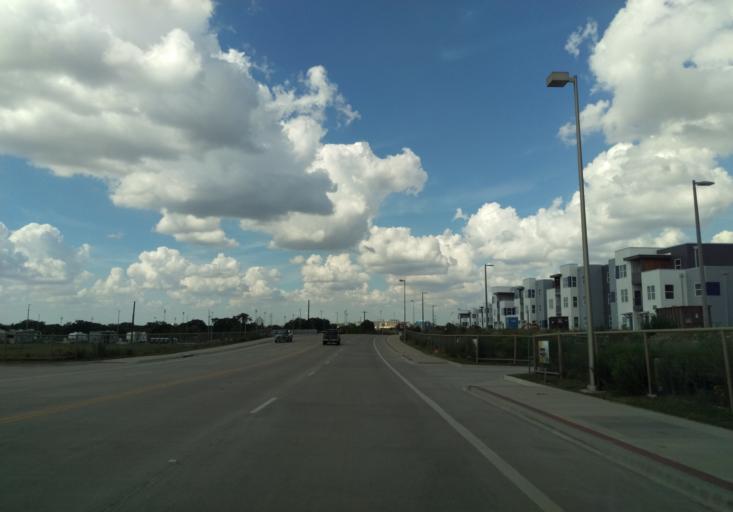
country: US
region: Texas
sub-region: Brazos County
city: College Station
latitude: 30.5957
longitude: -96.3411
